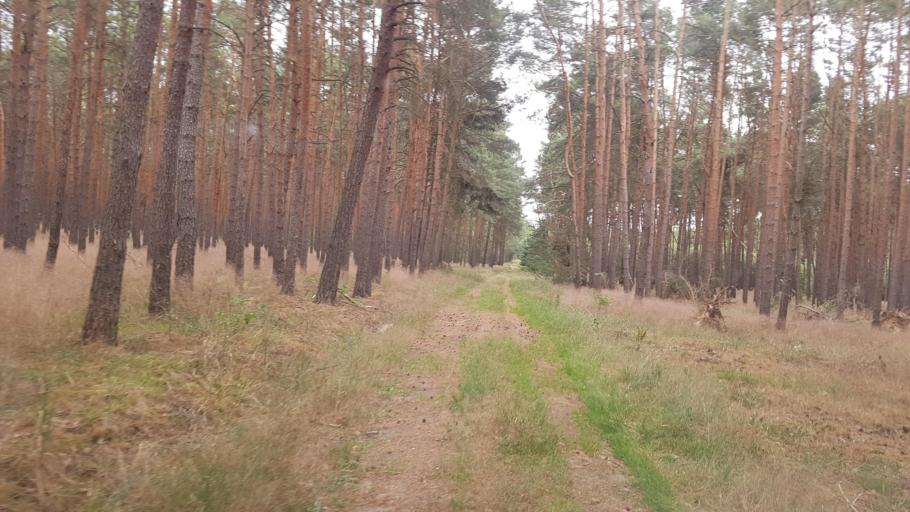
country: DE
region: Brandenburg
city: Treuenbrietzen
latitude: 52.0442
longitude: 12.8222
